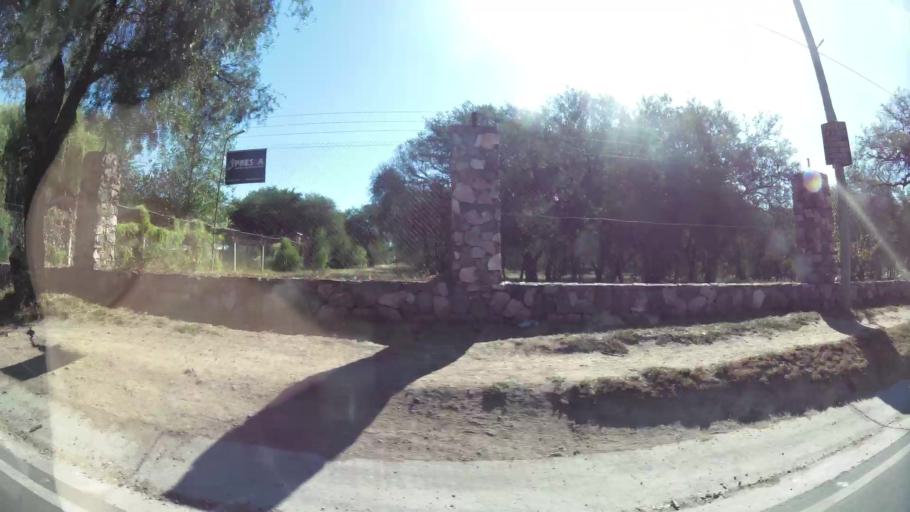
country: AR
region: Cordoba
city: La Calera
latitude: -31.3508
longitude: -64.3101
